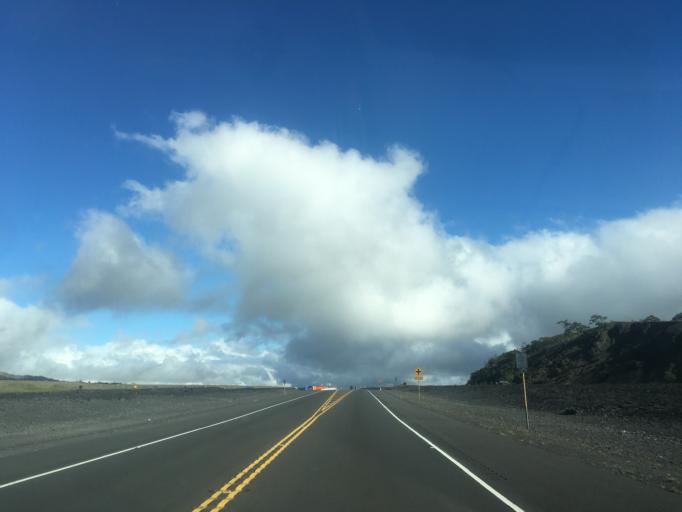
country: US
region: Hawaii
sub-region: Hawaii County
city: Volcano
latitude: 19.6891
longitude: -155.4701
